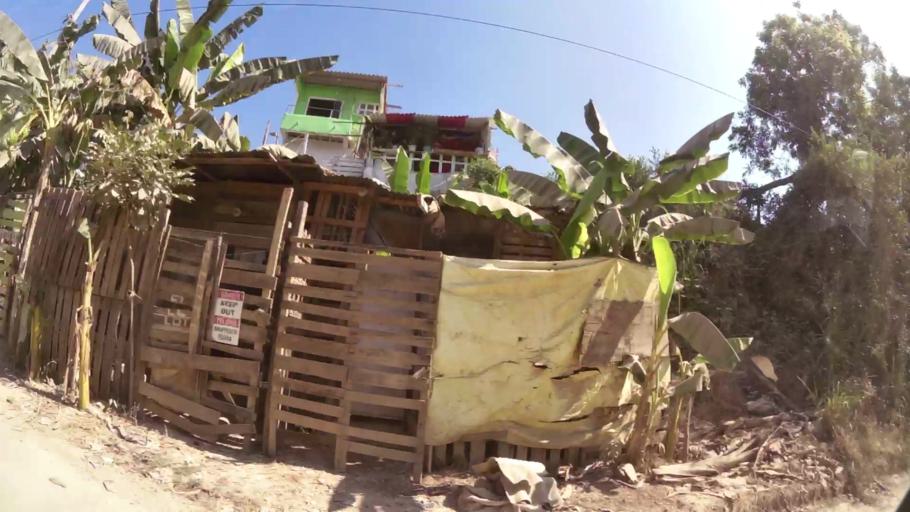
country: CO
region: Bolivar
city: Cartagena
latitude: 10.3708
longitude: -75.4947
